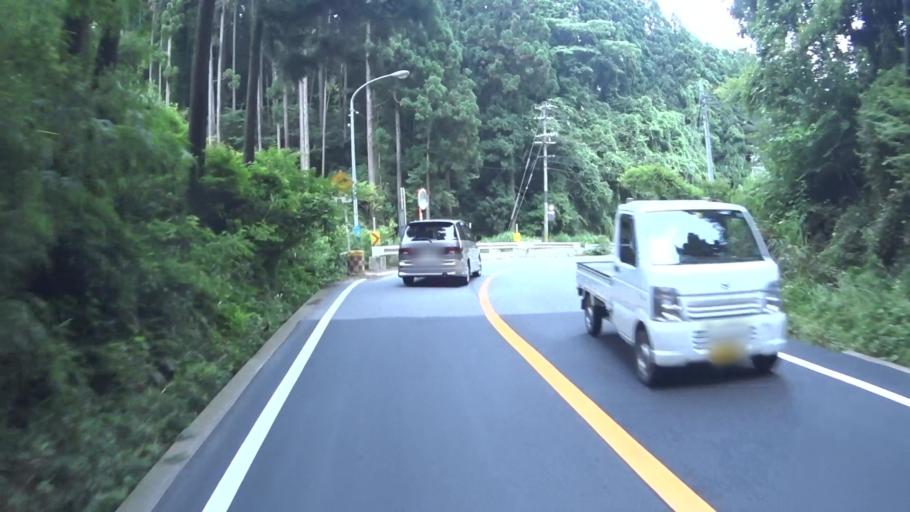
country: JP
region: Kyoto
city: Uji
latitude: 34.9138
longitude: 135.7496
